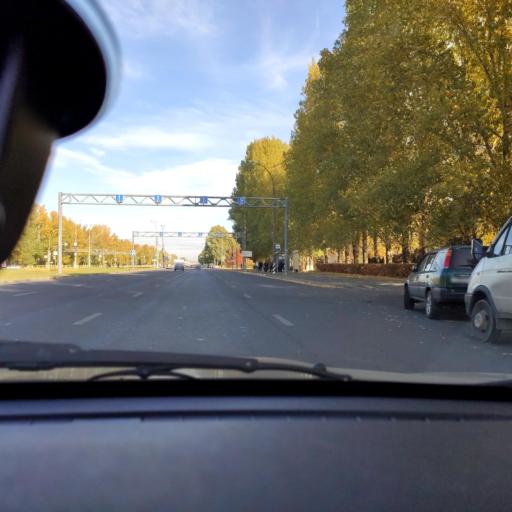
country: RU
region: Samara
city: Tol'yatti
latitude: 53.5053
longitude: 49.2762
